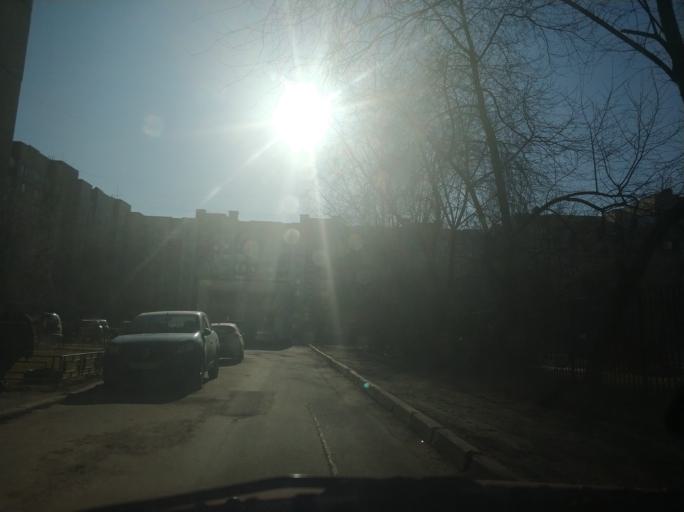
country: RU
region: St.-Petersburg
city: Krasnogvargeisky
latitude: 59.9507
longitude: 30.4818
